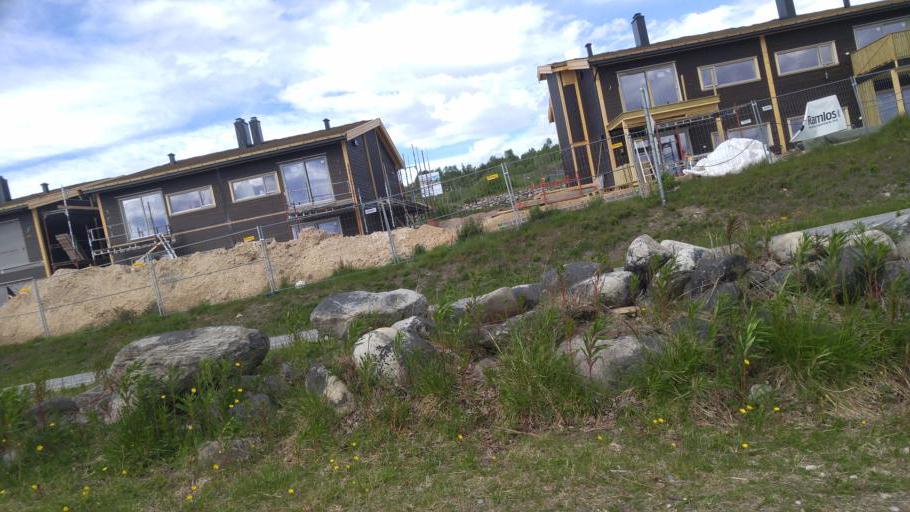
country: NO
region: Sor-Trondelag
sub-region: Roros
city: Roros
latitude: 62.5799
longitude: 11.3800
